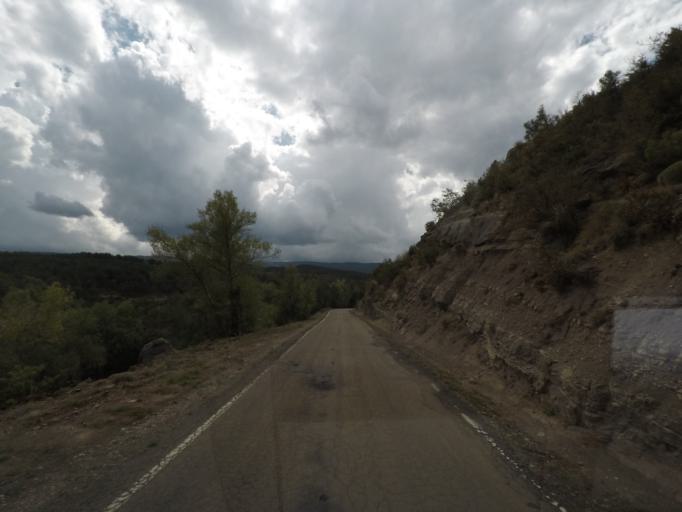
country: ES
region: Aragon
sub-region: Provincia de Huesca
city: Yebra de Basa
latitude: 42.3933
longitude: -0.2702
